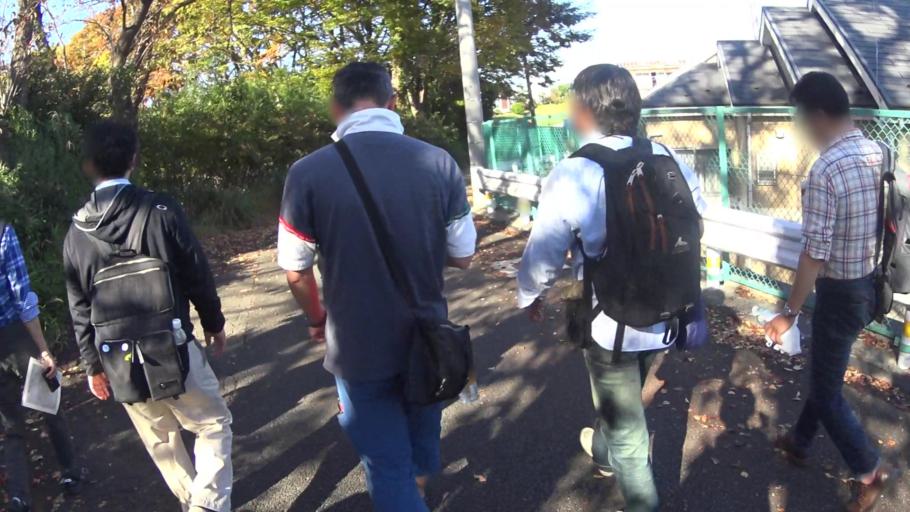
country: JP
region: Tokyo
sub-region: Machida-shi
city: Machida
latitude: 35.5681
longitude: 139.4406
